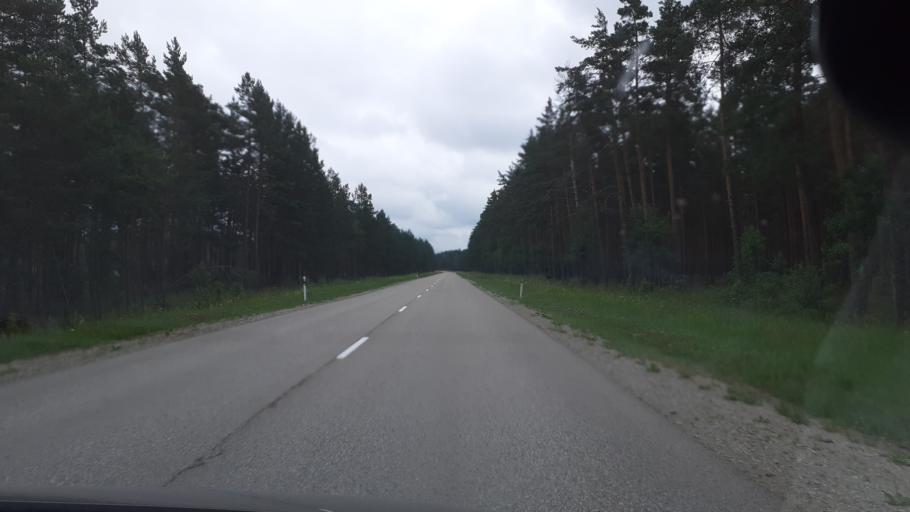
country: LV
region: Ventspils Rajons
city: Piltene
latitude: 57.1242
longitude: 21.7397
